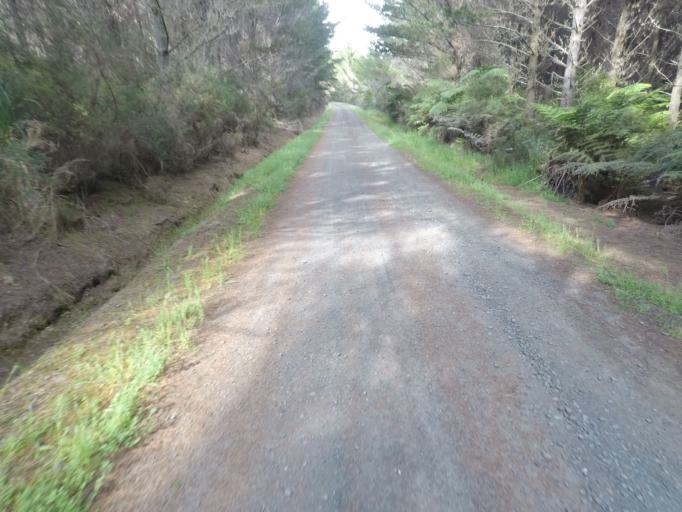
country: NZ
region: Auckland
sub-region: Auckland
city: Muriwai Beach
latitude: -36.7406
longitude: 174.5728
